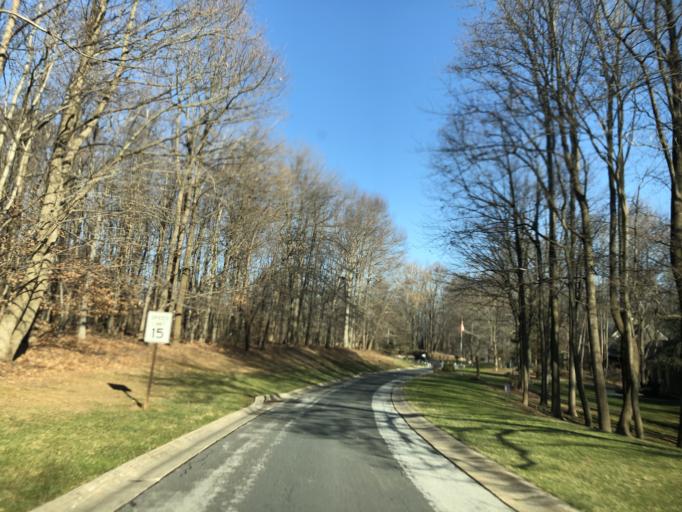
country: US
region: Pennsylvania
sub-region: Chester County
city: Downingtown
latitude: 39.9912
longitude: -75.7077
